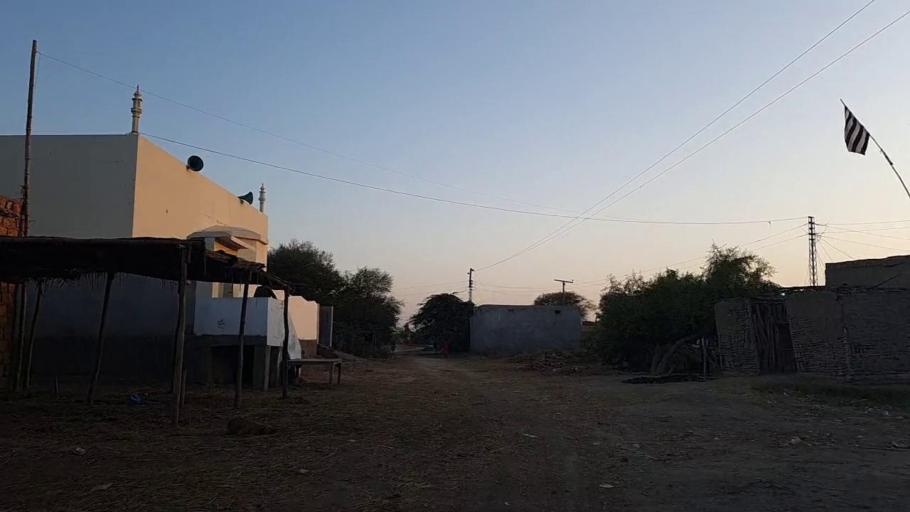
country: PK
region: Sindh
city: Mirpur Batoro
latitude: 24.6447
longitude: 68.1899
